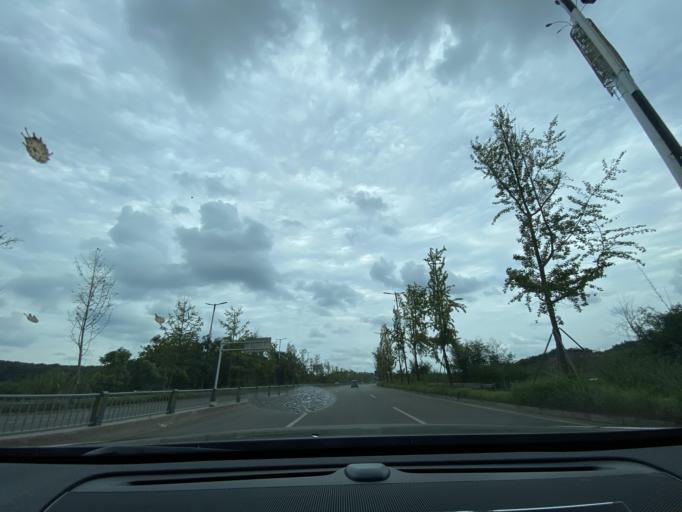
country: CN
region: Sichuan
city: Jiancheng
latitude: 30.4939
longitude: 104.4643
